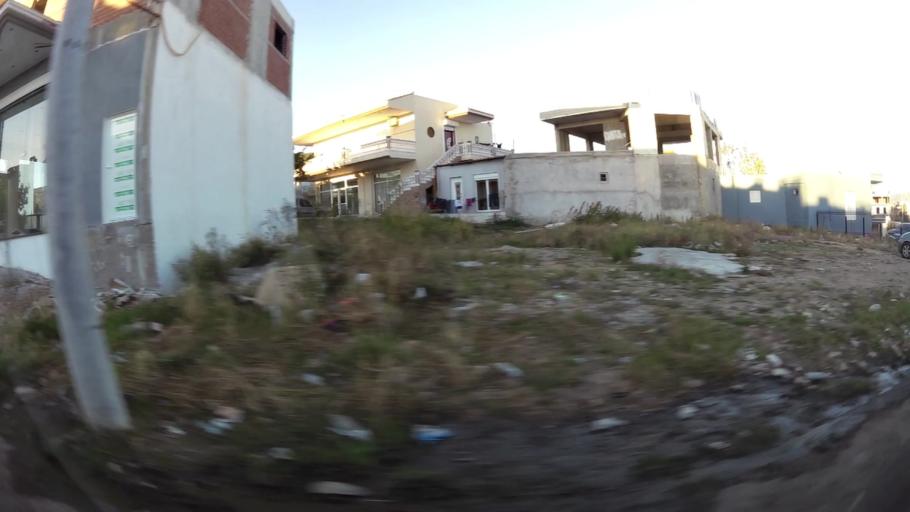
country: GR
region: Attica
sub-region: Nomarchia Dytikis Attikis
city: Ano Liosia
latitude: 38.0907
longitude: 23.6929
